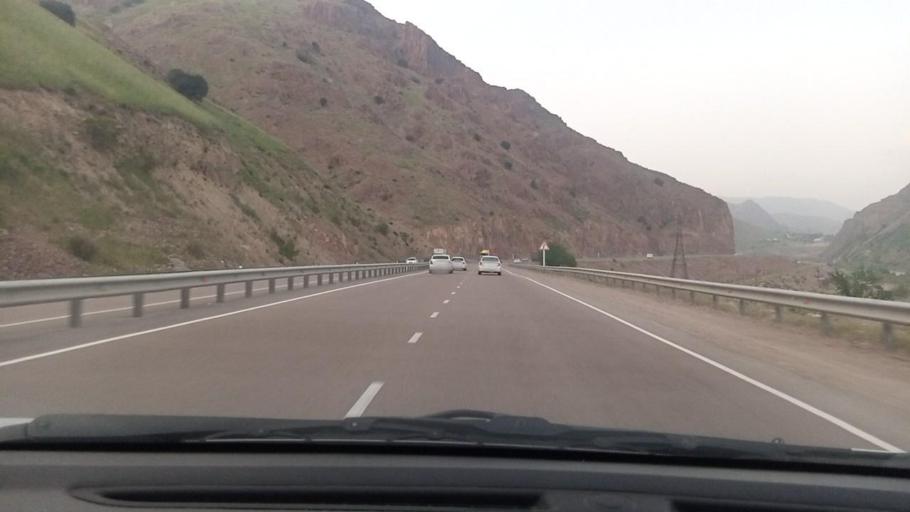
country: UZ
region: Toshkent
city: Angren
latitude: 41.1135
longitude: 70.3393
